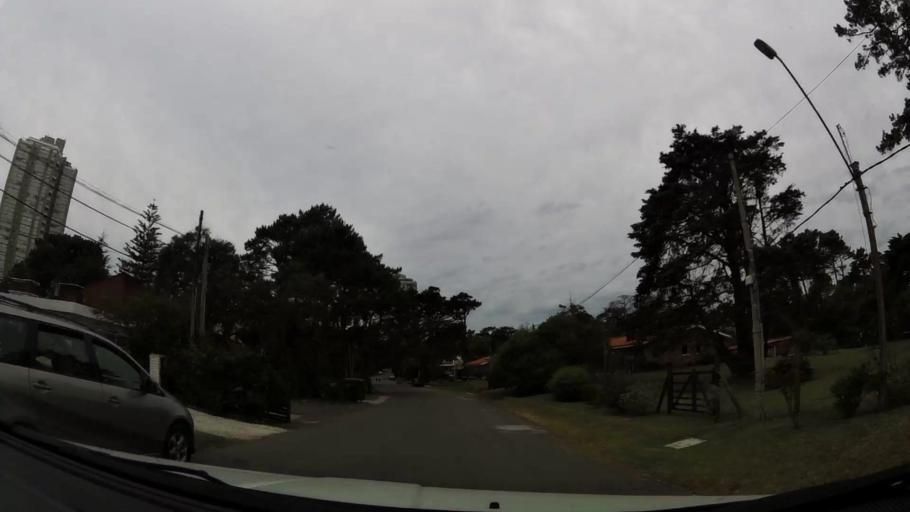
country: UY
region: Maldonado
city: Maldonado
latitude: -34.9224
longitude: -54.9559
